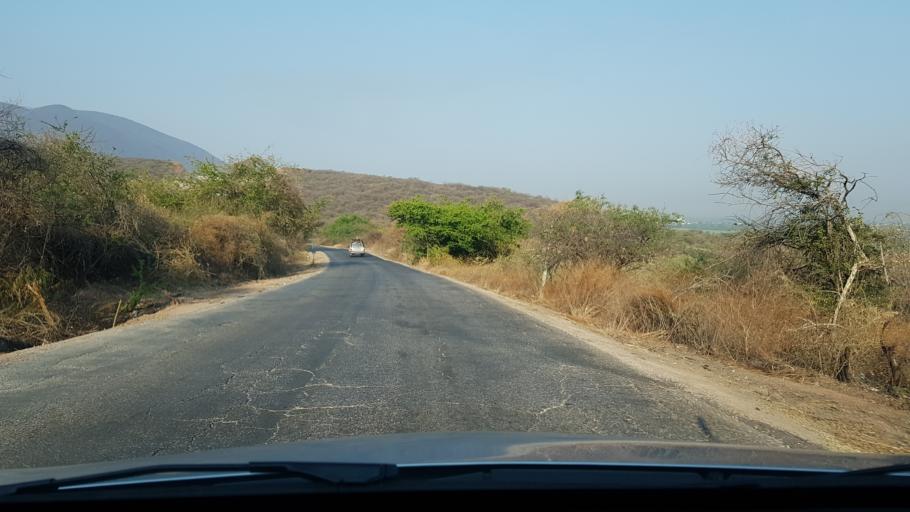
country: MX
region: Morelos
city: Tlaltizapan
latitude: 18.6787
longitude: -99.0834
